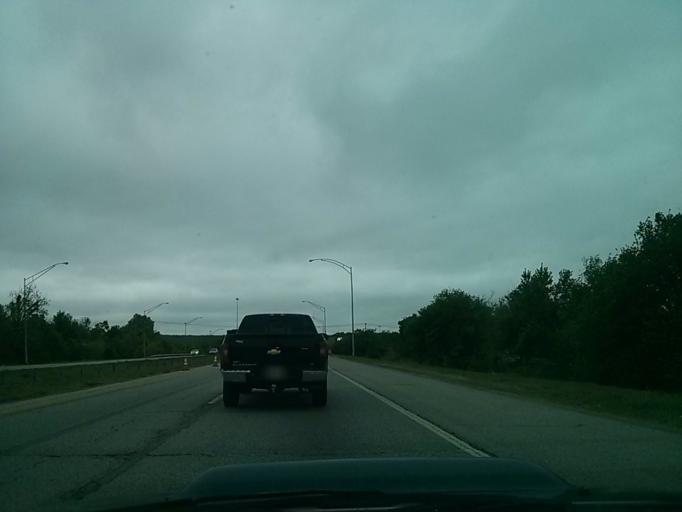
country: US
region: Oklahoma
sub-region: Tulsa County
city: Oakhurst
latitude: 36.0943
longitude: -96.0069
